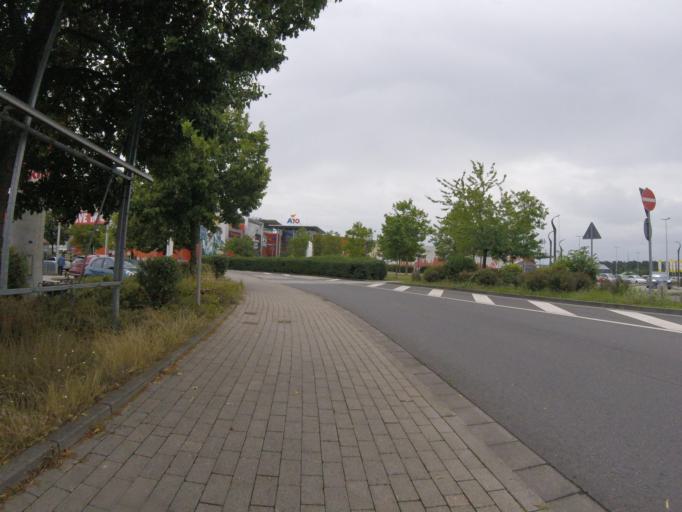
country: DE
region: Brandenburg
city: Wildau
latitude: 52.3146
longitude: 13.6048
